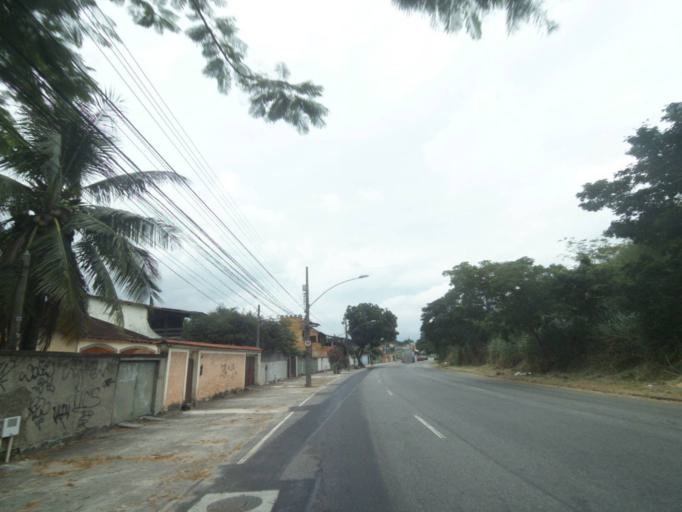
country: BR
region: Rio de Janeiro
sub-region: Nilopolis
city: Nilopolis
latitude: -22.8912
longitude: -43.3927
